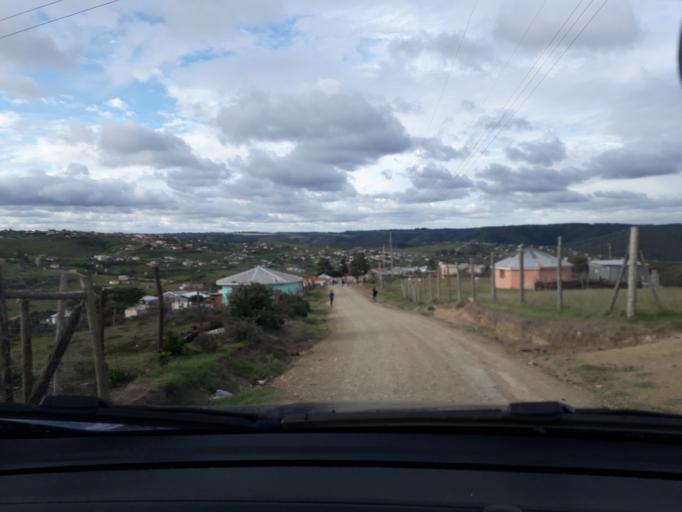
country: ZA
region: Eastern Cape
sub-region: Buffalo City Metropolitan Municipality
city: East London
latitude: -32.8056
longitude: 27.9592
